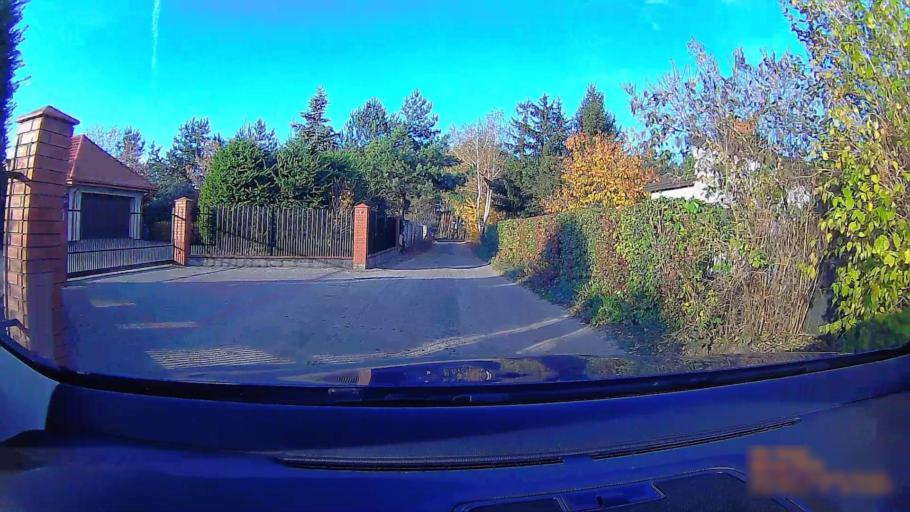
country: PL
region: Greater Poland Voivodeship
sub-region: Powiat koninski
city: Stare Miasto
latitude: 52.2032
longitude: 18.2050
